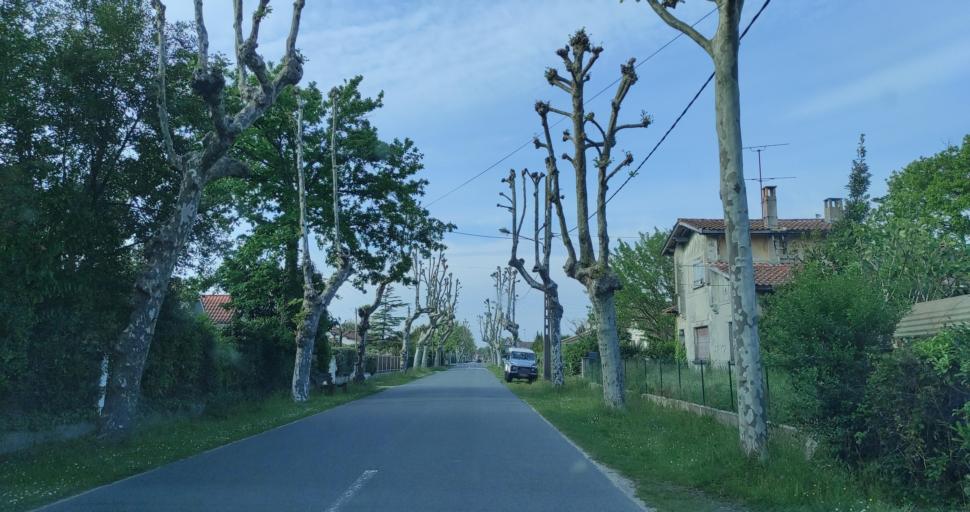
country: FR
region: Aquitaine
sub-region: Departement de la Gironde
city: Ares
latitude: 44.7614
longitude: -1.1326
